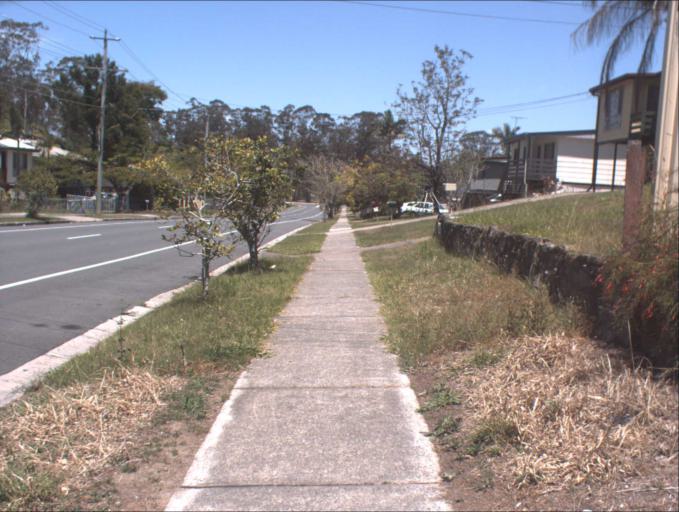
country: AU
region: Queensland
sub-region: Logan
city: Logan City
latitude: -27.6620
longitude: 153.1083
